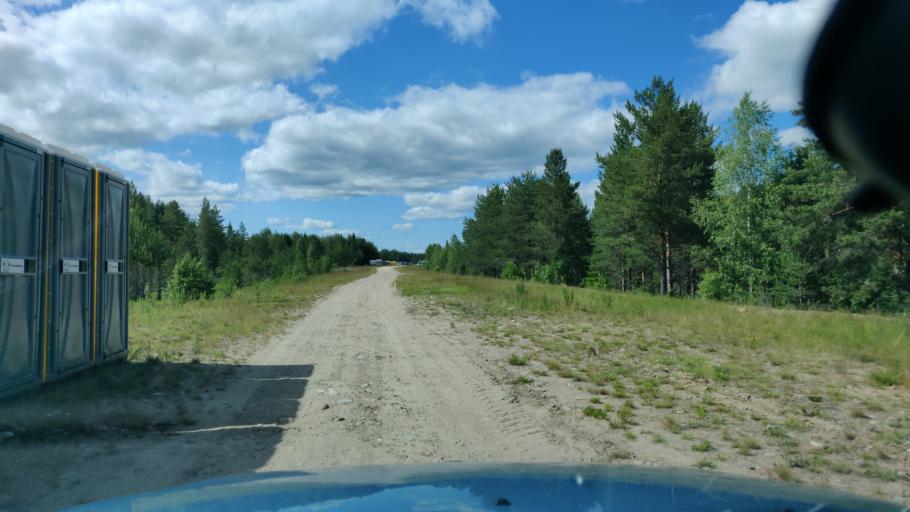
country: NO
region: Hedmark
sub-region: Trysil
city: Innbygda
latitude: 60.9062
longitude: 12.5721
